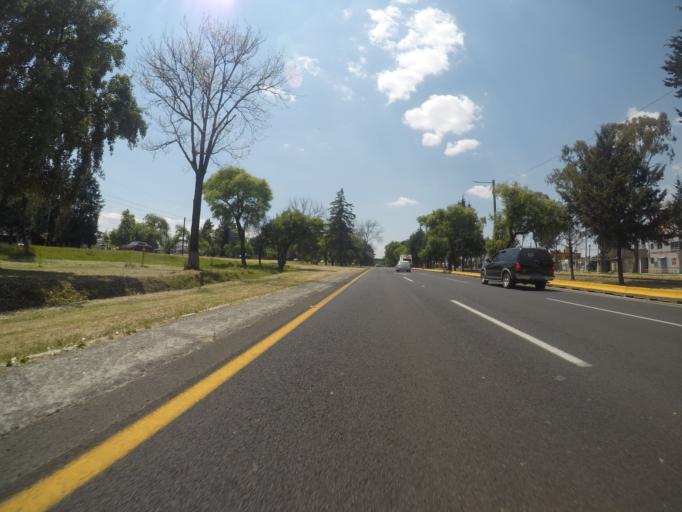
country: MX
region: Mexico
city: Santa Maria Totoltepec
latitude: 19.2871
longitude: -99.5816
